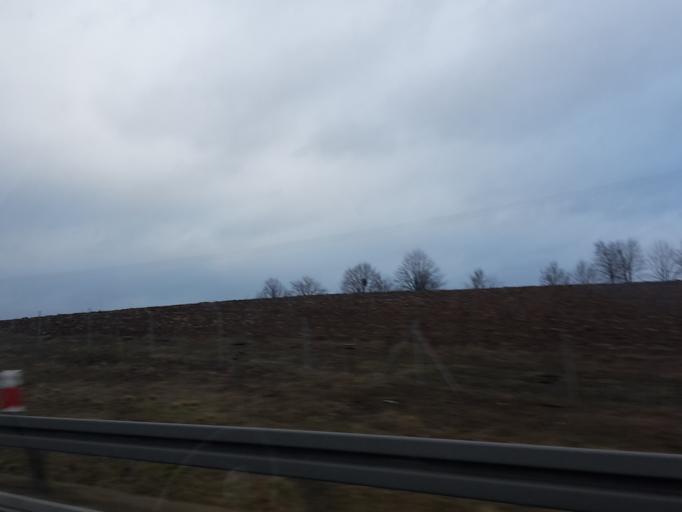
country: PL
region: Warmian-Masurian Voivodeship
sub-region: Powiat ostrodzki
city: Maldyty
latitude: 53.8538
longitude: 19.7506
